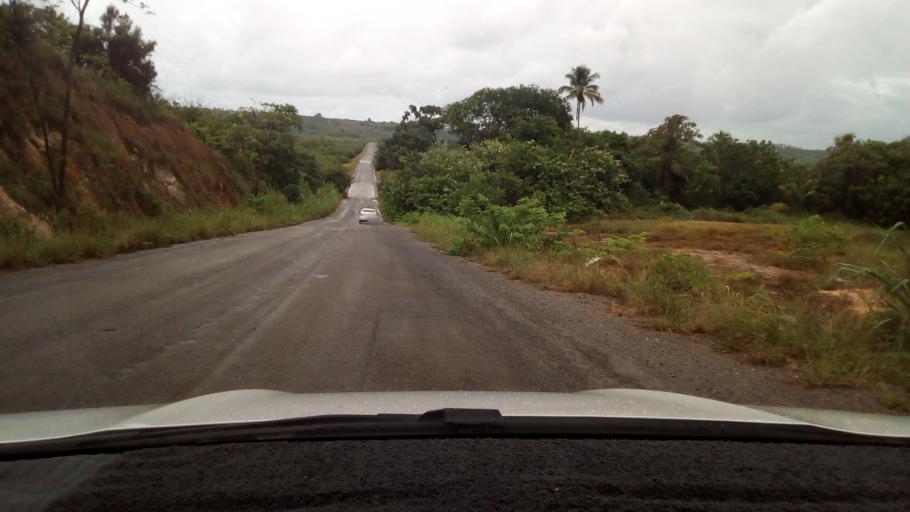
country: BR
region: Paraiba
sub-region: Pitimbu
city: Pitimbu
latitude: -7.4308
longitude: -34.8383
